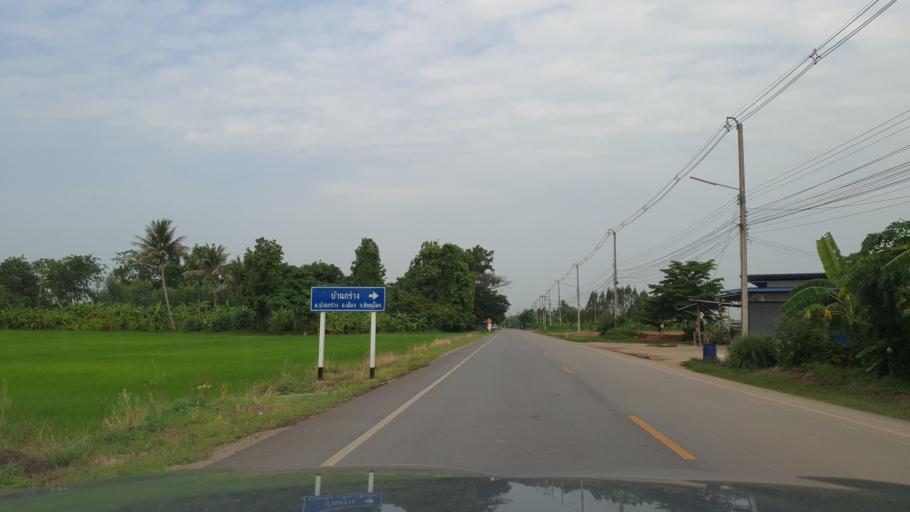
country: TH
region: Phitsanulok
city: Phitsanulok
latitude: 16.8145
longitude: 100.1830
